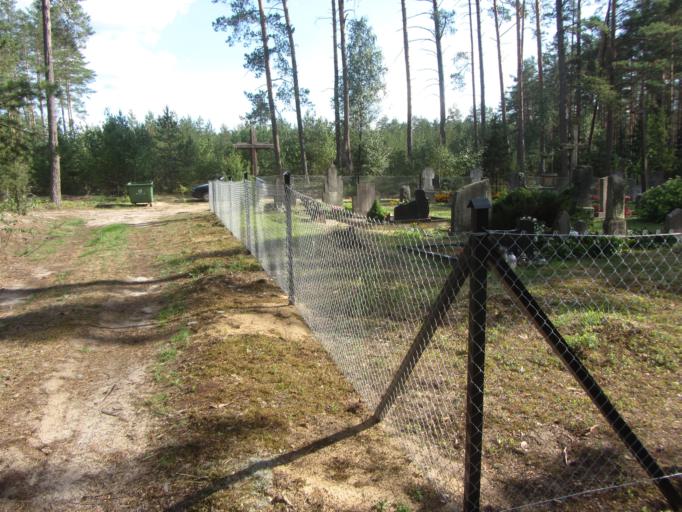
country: LT
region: Alytaus apskritis
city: Druskininkai
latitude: 54.0665
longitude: 24.2308
